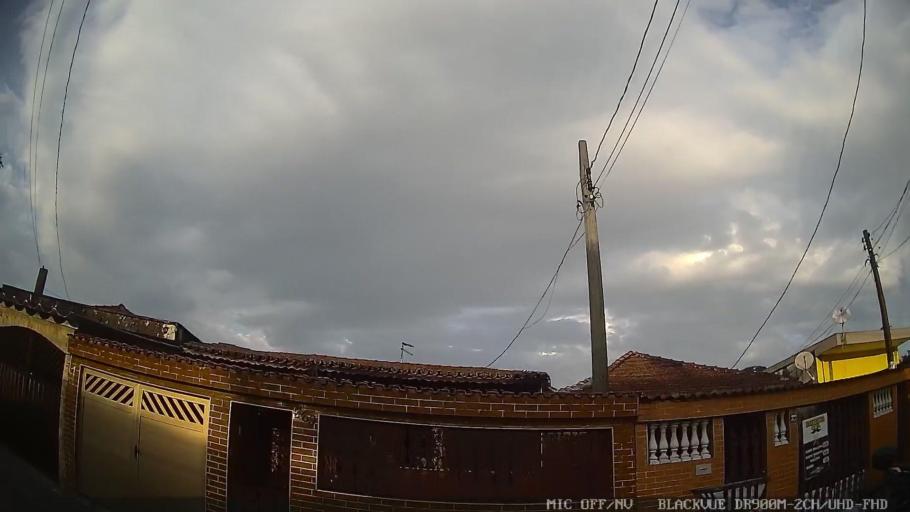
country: BR
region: Sao Paulo
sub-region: Cubatao
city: Cubatao
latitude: -23.8957
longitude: -46.4294
